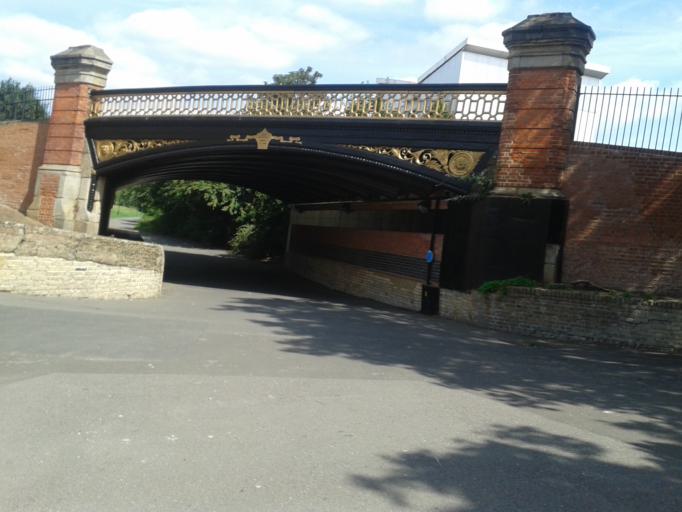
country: GB
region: England
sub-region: Greater London
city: Camberwell
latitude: 51.4798
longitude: -0.0723
